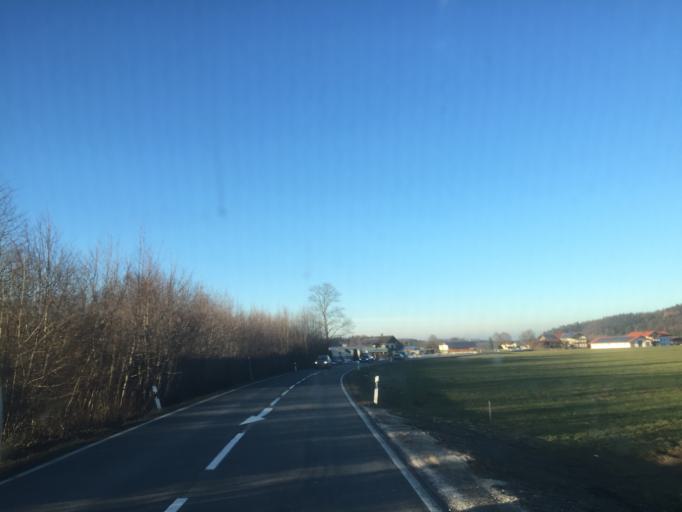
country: DE
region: Bavaria
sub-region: Upper Bavaria
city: Siegsdorf
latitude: 47.8338
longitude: 12.6350
